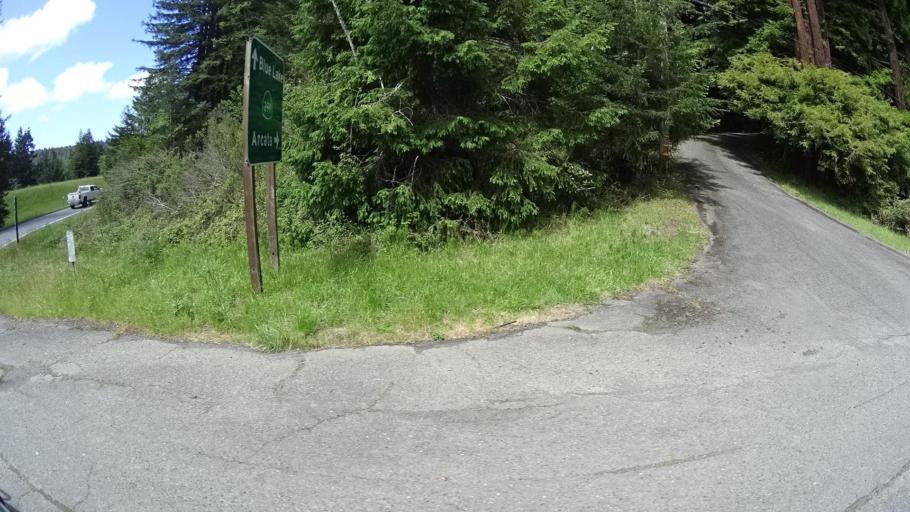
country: US
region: California
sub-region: Humboldt County
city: Blue Lake
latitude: 40.9077
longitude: -124.0373
